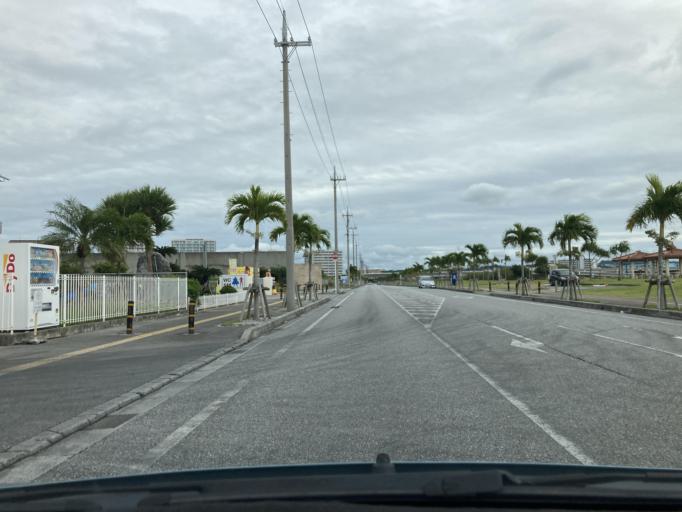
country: JP
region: Okinawa
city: Itoman
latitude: 26.1527
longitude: 127.6541
